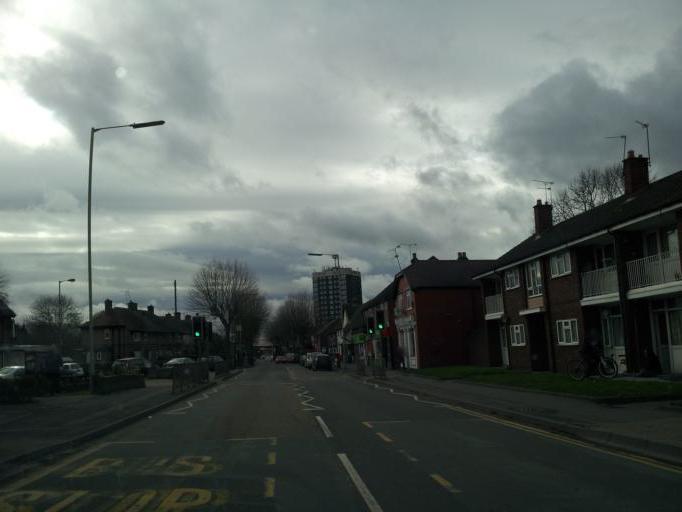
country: GB
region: England
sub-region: Staffordshire
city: Stafford
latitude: 52.8075
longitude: -2.1021
